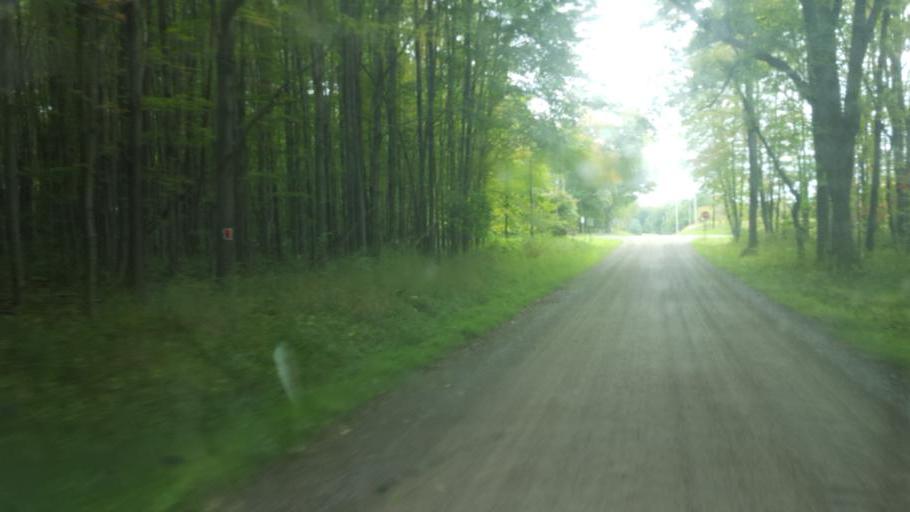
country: US
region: Pennsylvania
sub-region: Crawford County
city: Pymatuning Central
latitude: 41.5434
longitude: -80.4286
